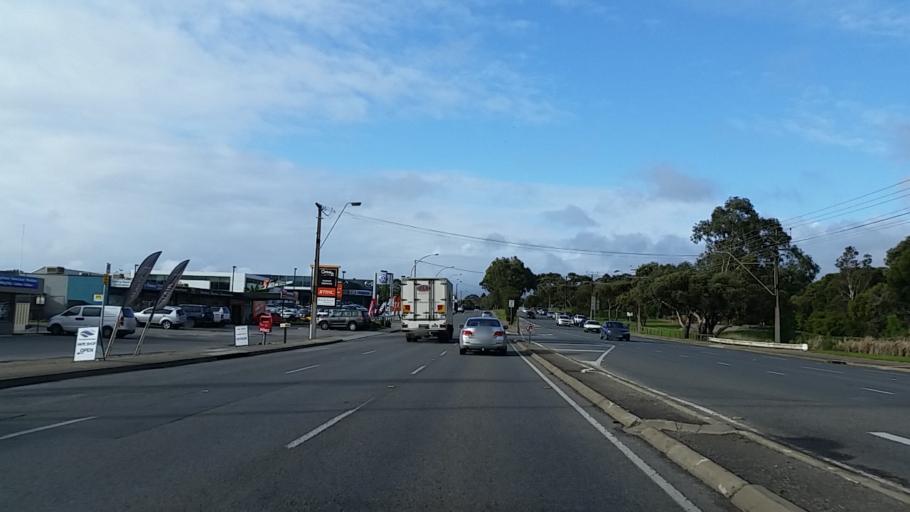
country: AU
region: South Australia
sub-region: Onkaparinga
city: Reynella
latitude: -35.1039
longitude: 138.5283
